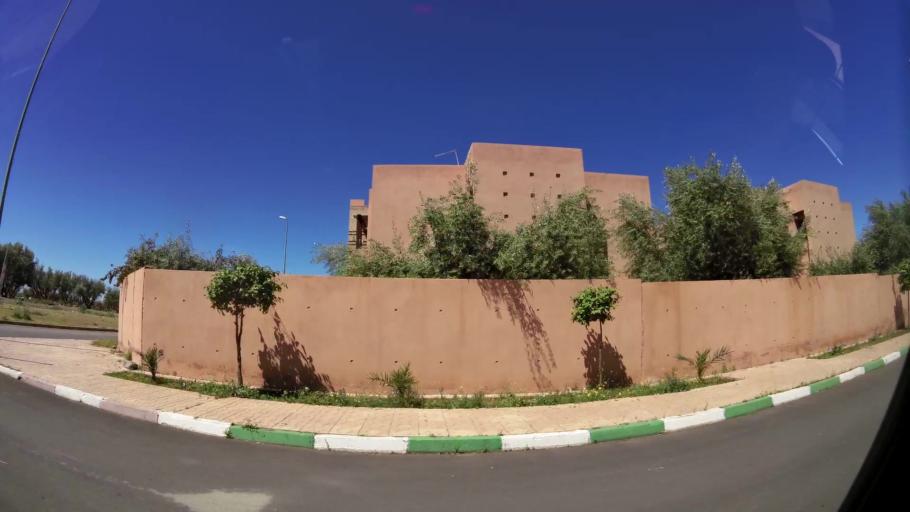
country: MA
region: Marrakech-Tensift-Al Haouz
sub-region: Marrakech
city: Marrakesh
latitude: 31.5698
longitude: -7.9847
